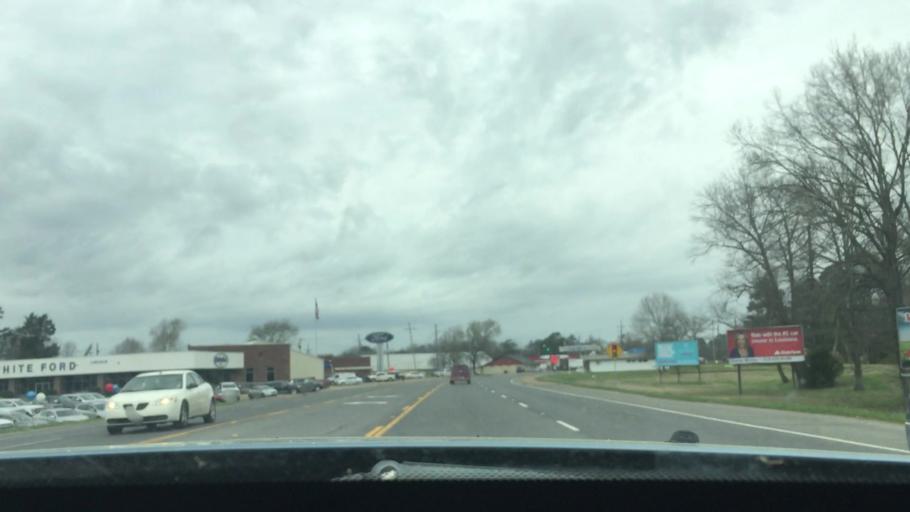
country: US
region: Louisiana
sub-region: Franklin Parish
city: Winnsboro
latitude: 32.1551
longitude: -91.7124
